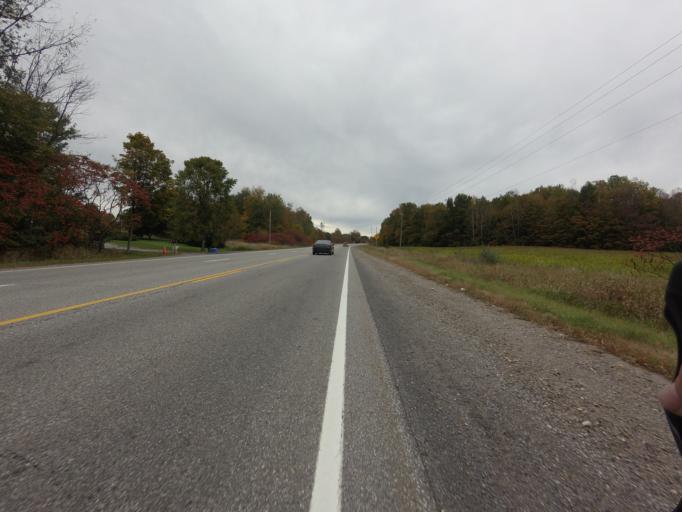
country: CA
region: Ontario
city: Gananoque
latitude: 44.4384
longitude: -76.2816
